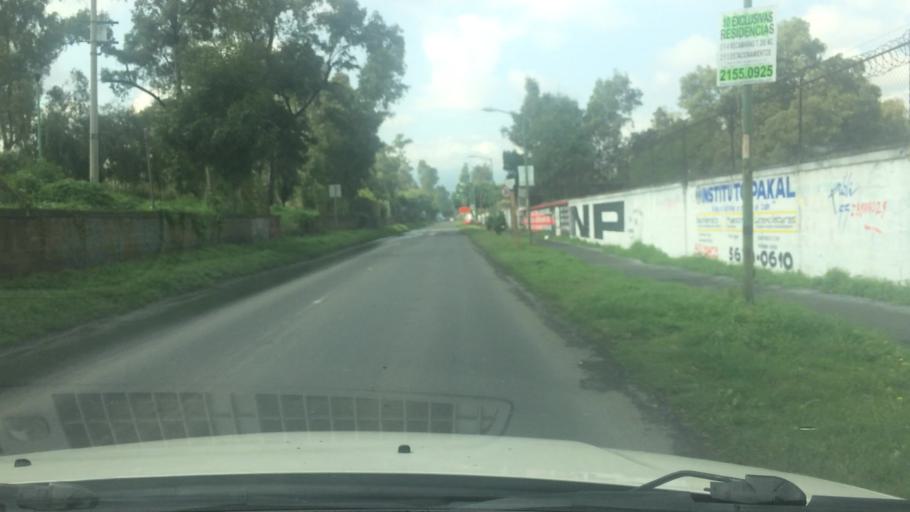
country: MX
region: Mexico City
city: Xochimilco
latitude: 19.3046
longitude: -99.1005
